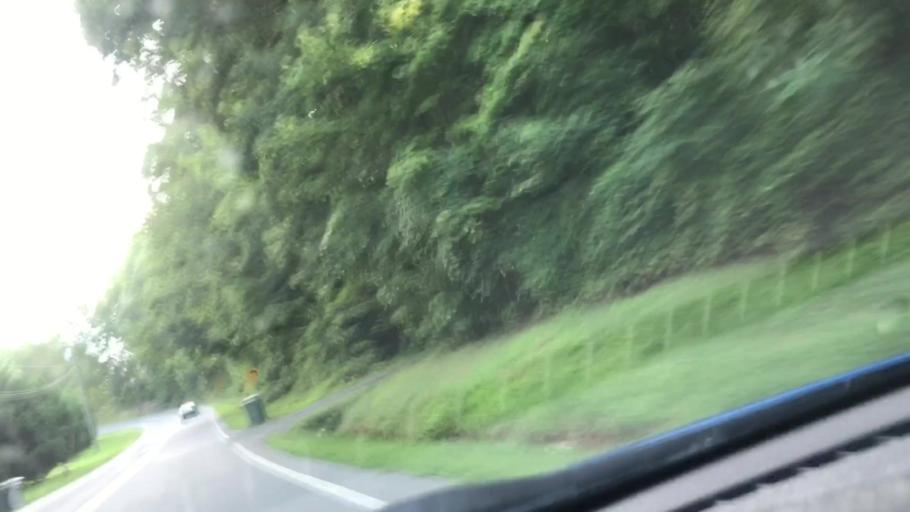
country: US
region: North Carolina
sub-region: Randolph County
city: Asheboro
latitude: 35.7284
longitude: -79.8041
